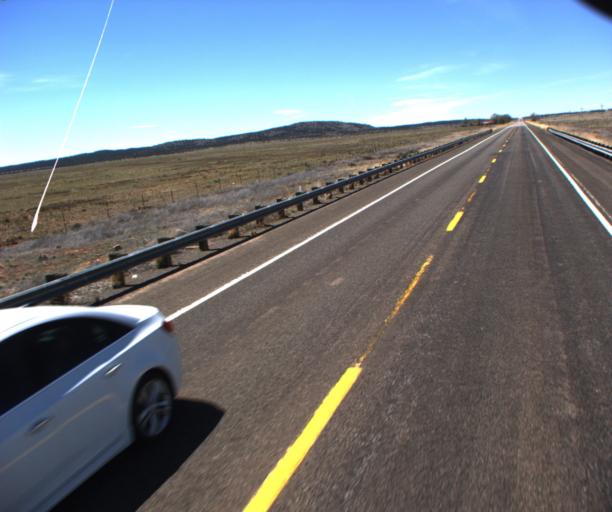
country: US
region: Arizona
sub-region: Mohave County
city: Peach Springs
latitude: 35.4727
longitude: -113.1288
